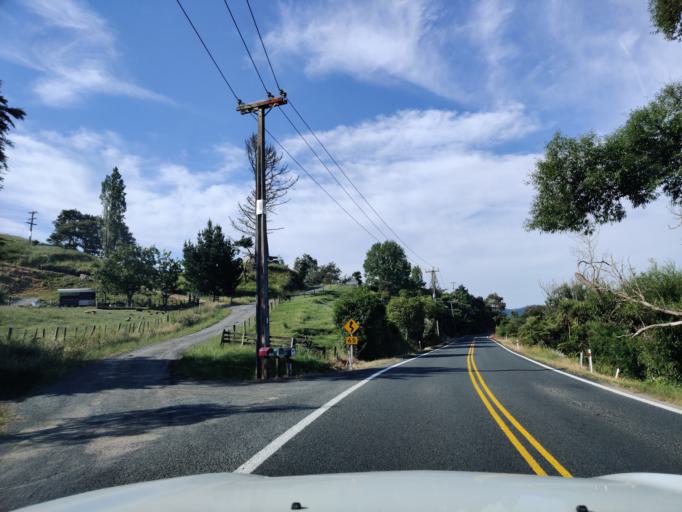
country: NZ
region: Waikato
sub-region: Waikato District
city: Ngaruawahia
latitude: -37.6547
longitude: 175.1426
